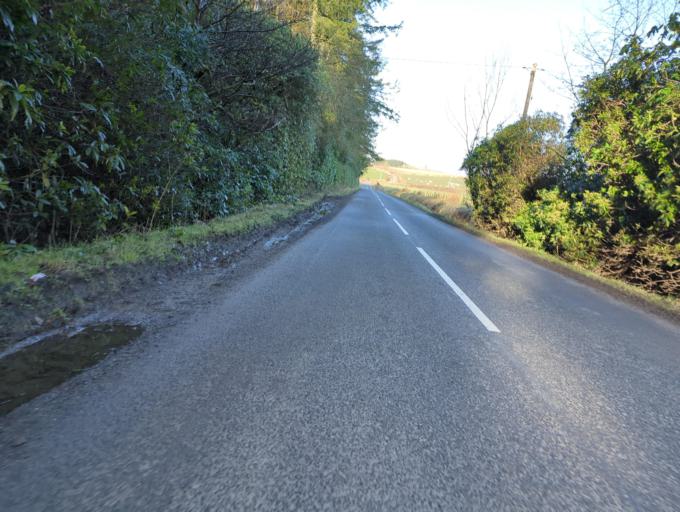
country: GB
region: Scotland
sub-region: Perth and Kinross
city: Methven
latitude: 56.4547
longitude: -3.5452
